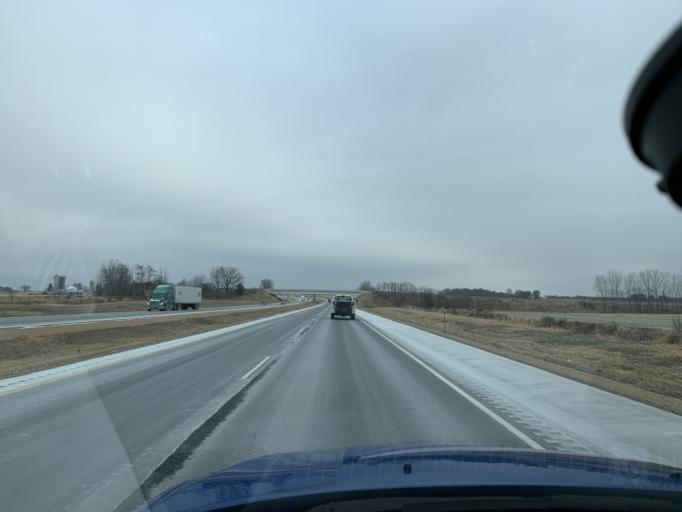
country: US
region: Wisconsin
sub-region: Columbia County
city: Columbus
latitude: 43.2772
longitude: -89.0920
